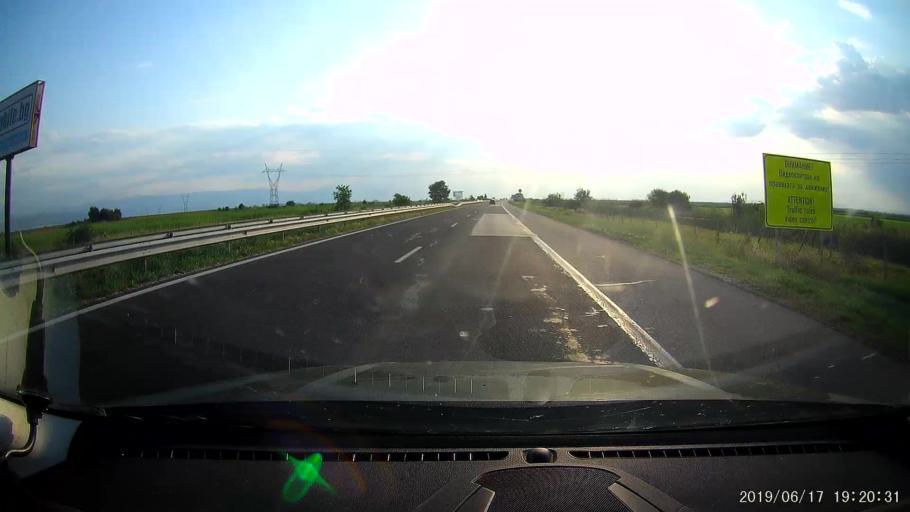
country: BG
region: Plovdiv
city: Stamboliyski
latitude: 42.2055
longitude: 24.4925
